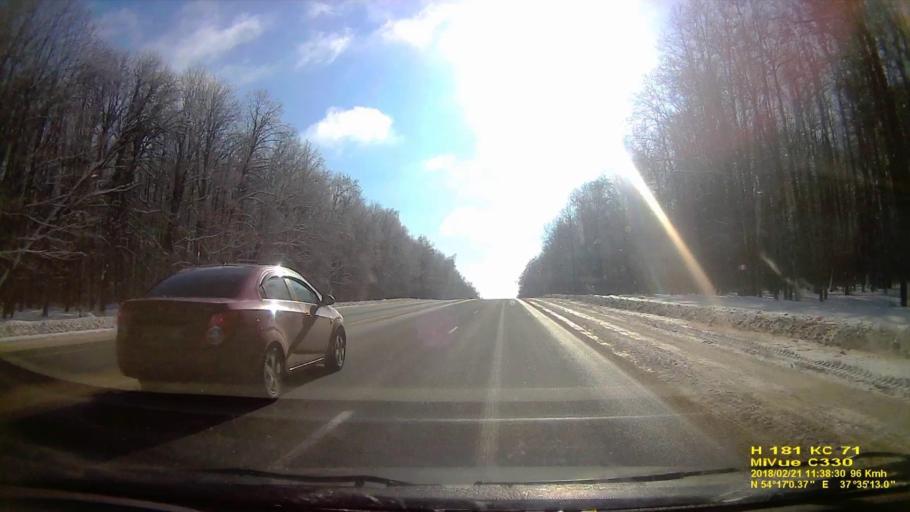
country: RU
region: Tula
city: Gorelki
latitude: 54.2831
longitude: 37.5872
